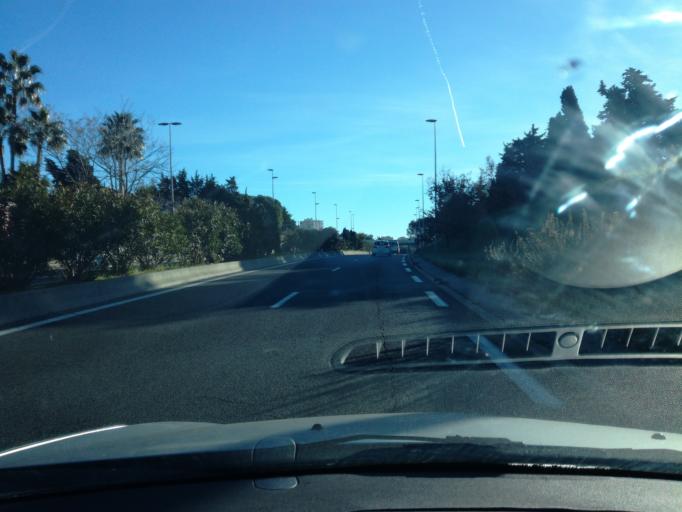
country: FR
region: Provence-Alpes-Cote d'Azur
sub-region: Departement des Alpes-Maritimes
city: Antibes
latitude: 43.5792
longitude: 7.0966
